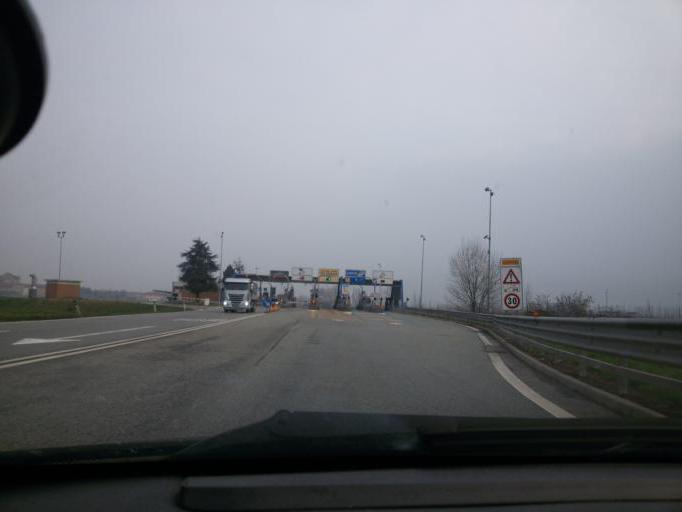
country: IT
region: Piedmont
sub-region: Provincia di Vercelli
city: Asigliano Vercellese
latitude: 45.2935
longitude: 8.3892
